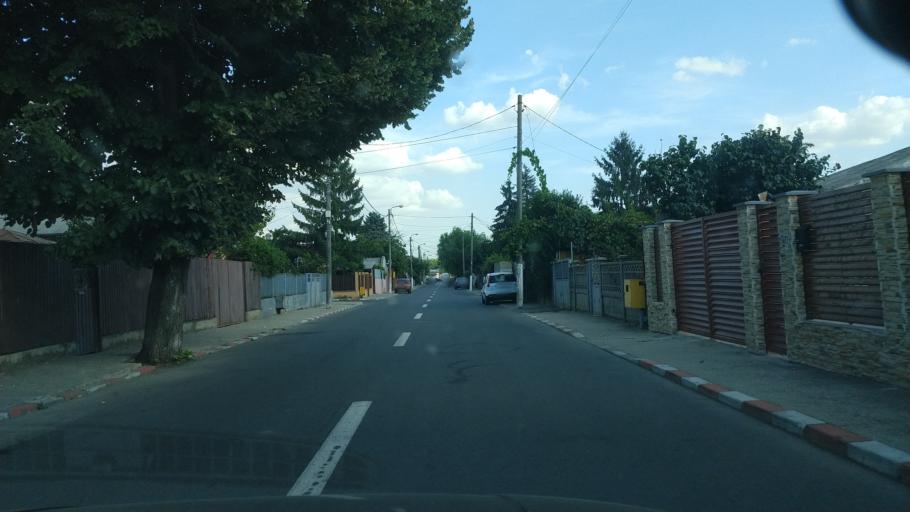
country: RO
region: Ilfov
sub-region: Voluntari City
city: Voluntari
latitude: 44.4908
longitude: 26.1667
